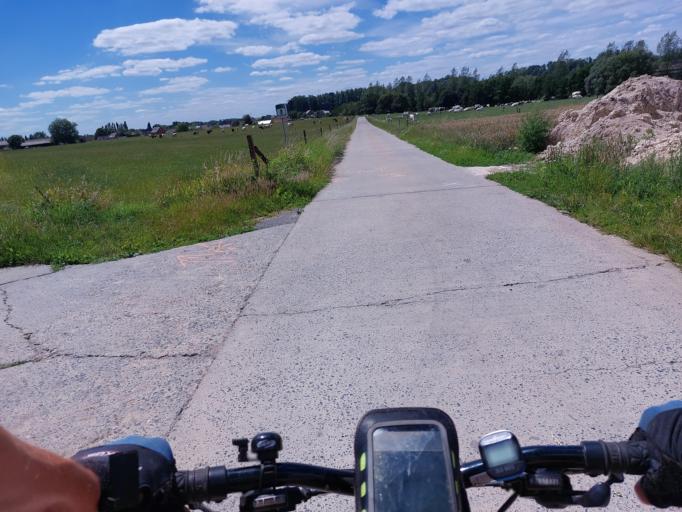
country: BE
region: Wallonia
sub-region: Province du Hainaut
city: Brugelette
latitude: 50.6111
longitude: 3.8959
